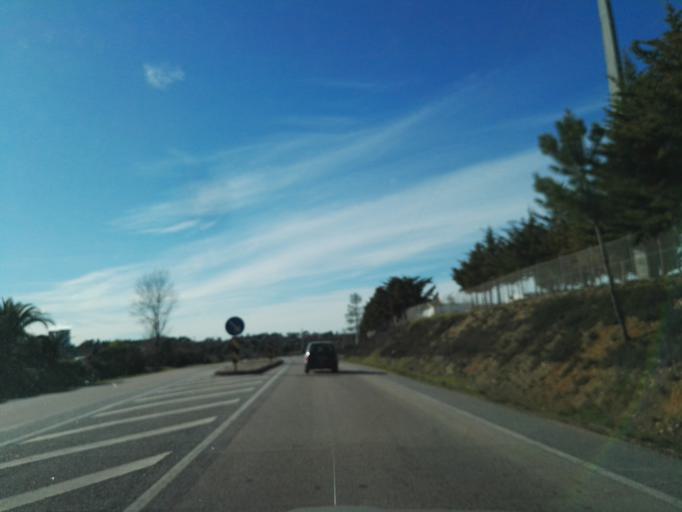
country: PT
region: Santarem
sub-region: Abrantes
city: Alferrarede
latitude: 39.4760
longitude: -8.0794
